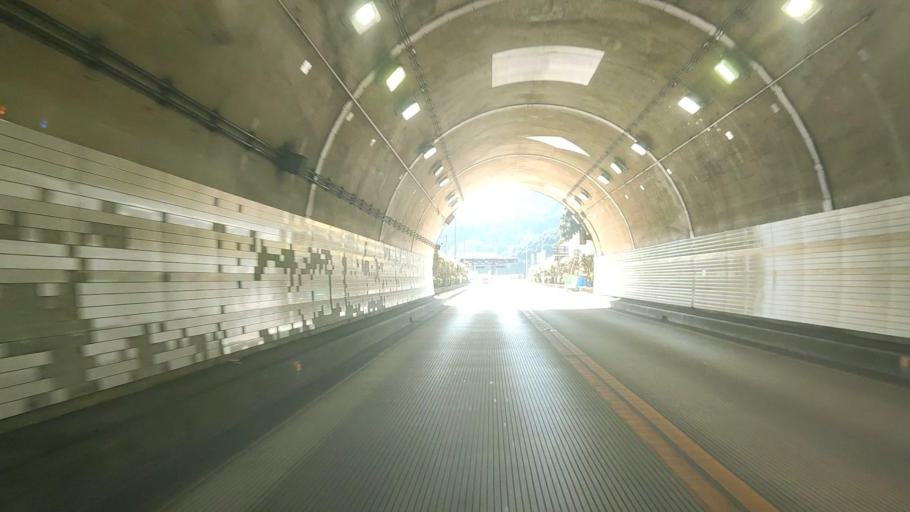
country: JP
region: Fukuoka
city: Maebaru-chuo
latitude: 33.4648
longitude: 130.2772
